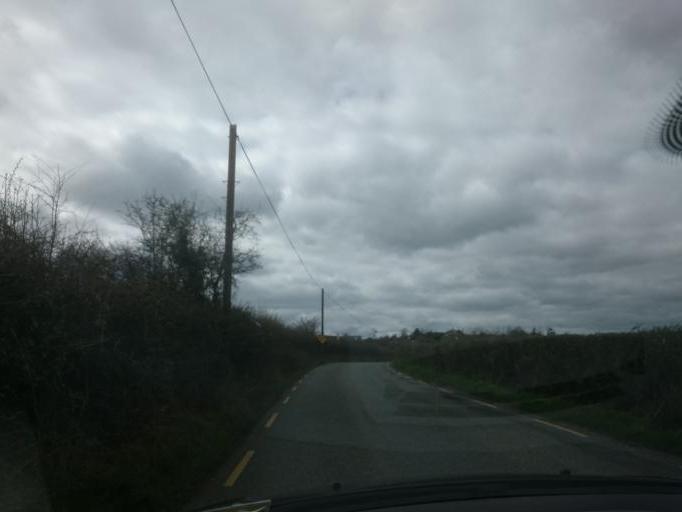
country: IE
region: Leinster
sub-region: Kilkenny
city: Kilkenny
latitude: 52.6713
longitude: -7.3631
